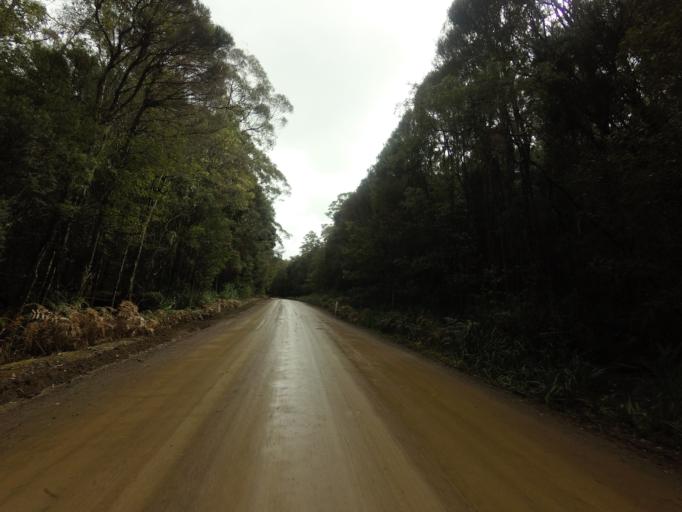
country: AU
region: Tasmania
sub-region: Huon Valley
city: Geeveston
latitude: -43.4090
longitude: 146.8719
